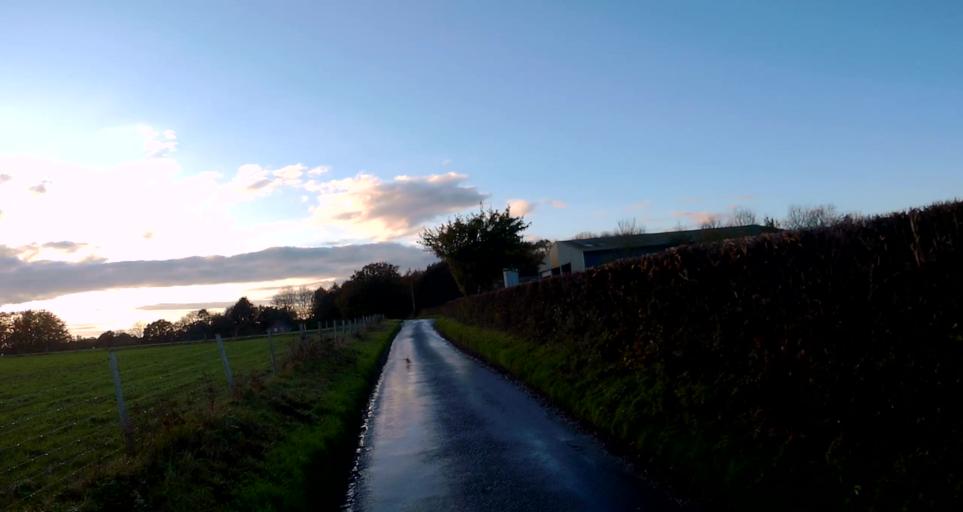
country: GB
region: England
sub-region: Hampshire
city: Basingstoke
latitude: 51.2148
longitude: -1.0975
